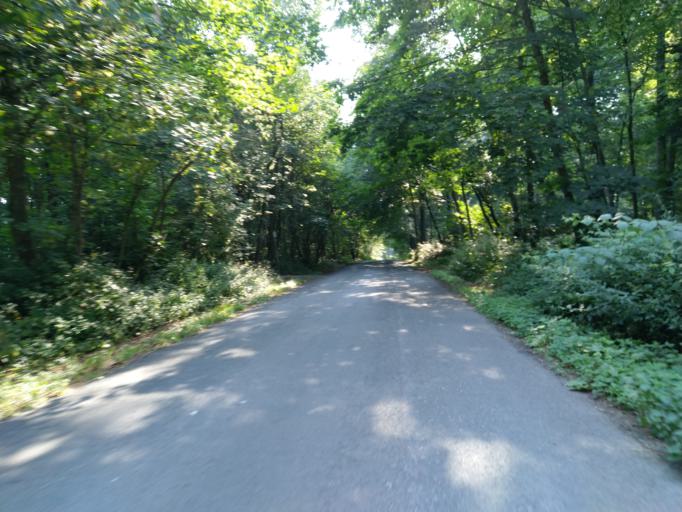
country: BE
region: Wallonia
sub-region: Province du Hainaut
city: Braine-le-Comte
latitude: 50.6094
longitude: 4.1847
